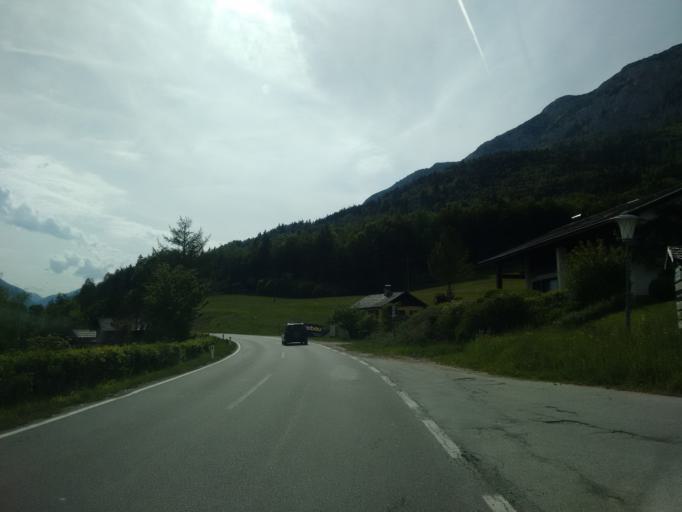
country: AT
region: Styria
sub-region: Politischer Bezirk Liezen
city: Bad Aussee
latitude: 47.6365
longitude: 13.8601
